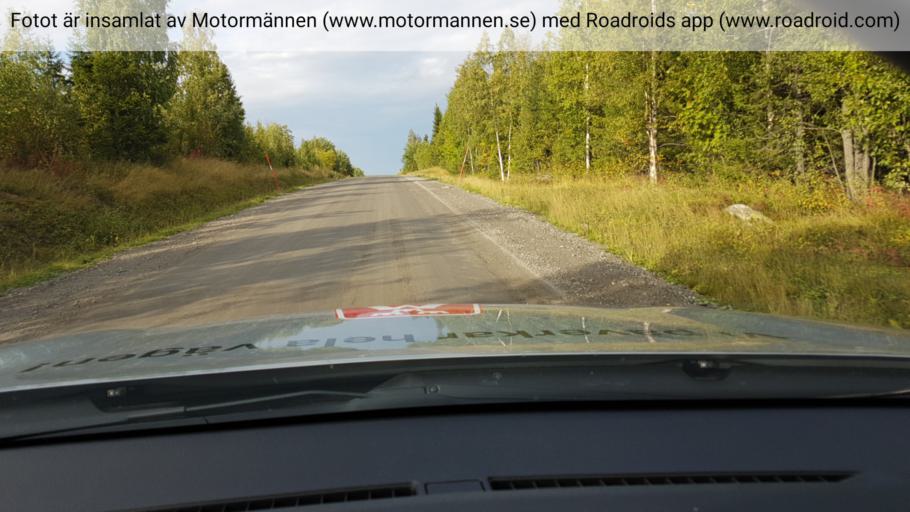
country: SE
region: Jaemtland
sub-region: Stroemsunds Kommun
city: Stroemsund
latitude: 64.0073
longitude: 15.8152
